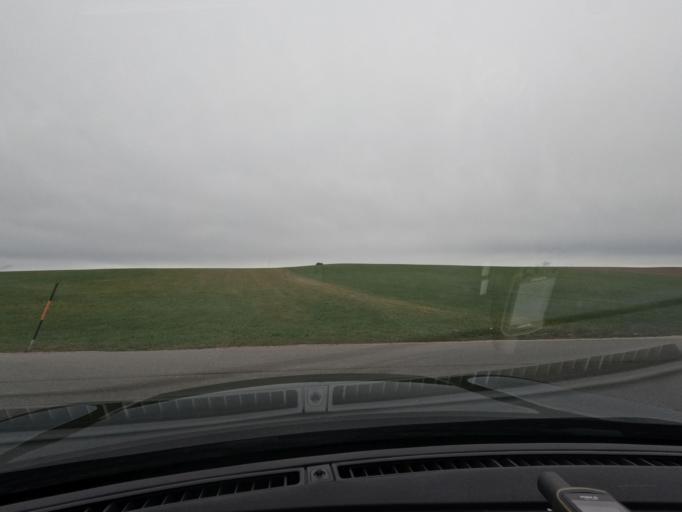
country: DE
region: Bavaria
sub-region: Upper Bavaria
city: Surberg
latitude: 47.8701
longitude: 12.6789
